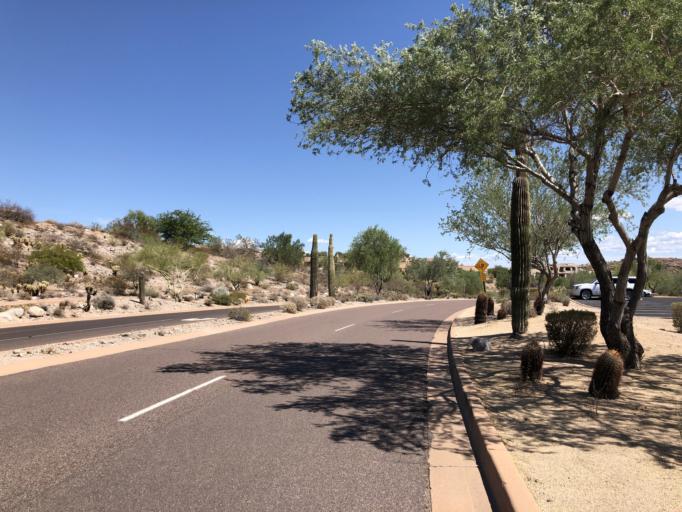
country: US
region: Arizona
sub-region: Maricopa County
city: Fountain Hills
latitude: 33.5772
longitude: -111.7600
